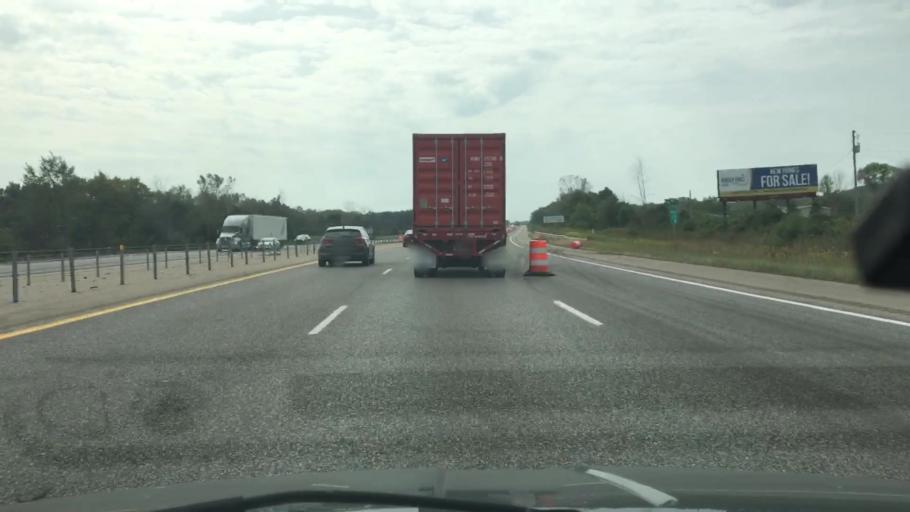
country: US
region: Michigan
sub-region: Berrien County
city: Bridgman
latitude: 41.9201
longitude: -86.5719
